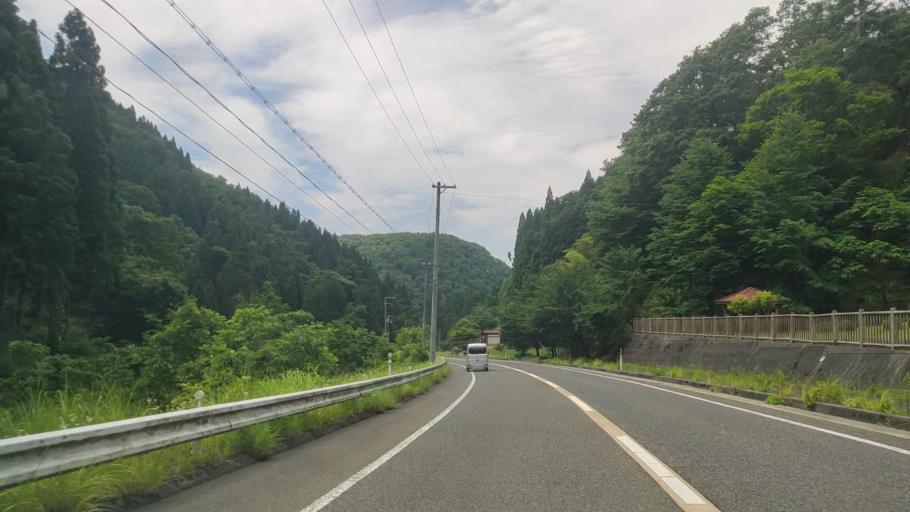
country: JP
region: Hyogo
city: Toyooka
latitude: 35.4876
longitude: 134.6163
